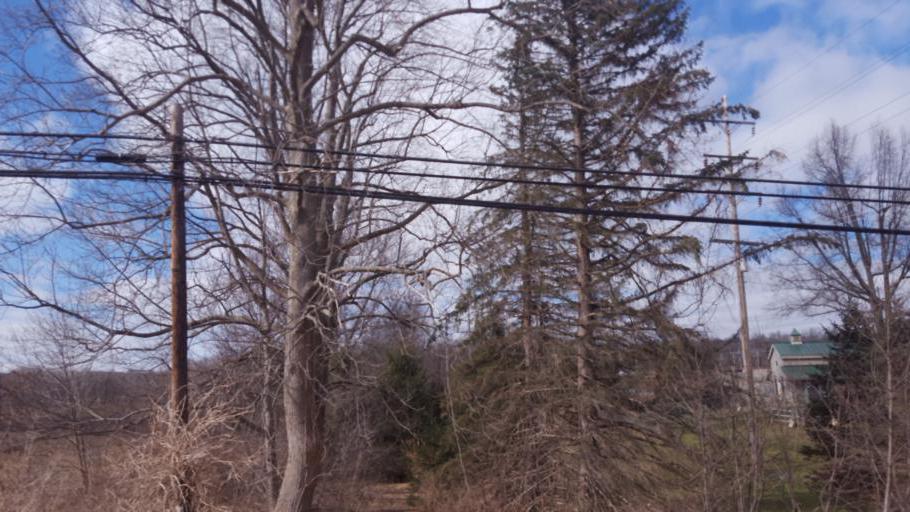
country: US
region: Ohio
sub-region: Richland County
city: Mansfield
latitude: 40.7194
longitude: -82.5122
